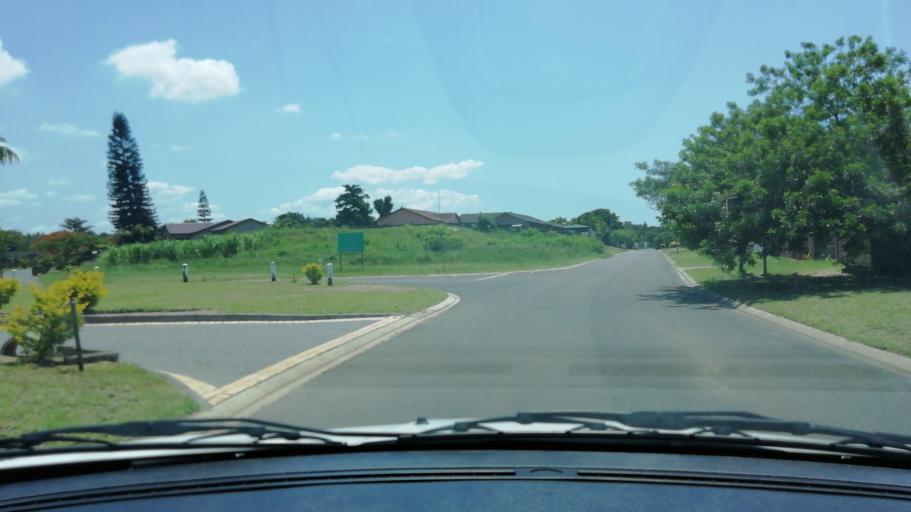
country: ZA
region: KwaZulu-Natal
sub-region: uThungulu District Municipality
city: Richards Bay
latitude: -28.7348
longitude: 32.0521
